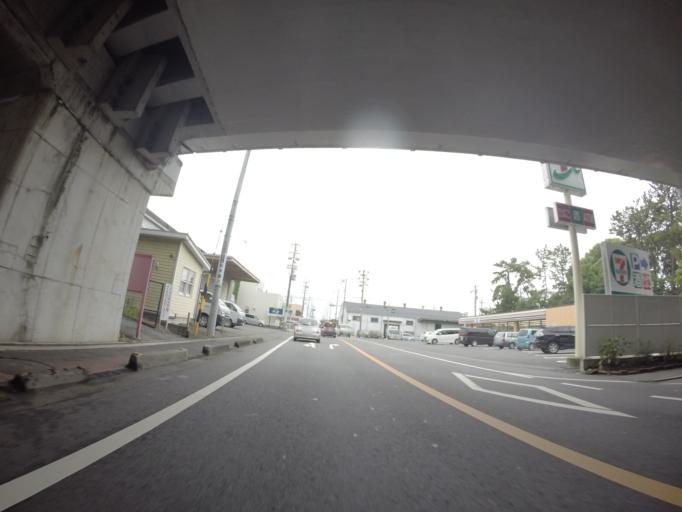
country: JP
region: Shizuoka
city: Shizuoka-shi
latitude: 34.9488
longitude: 138.3980
